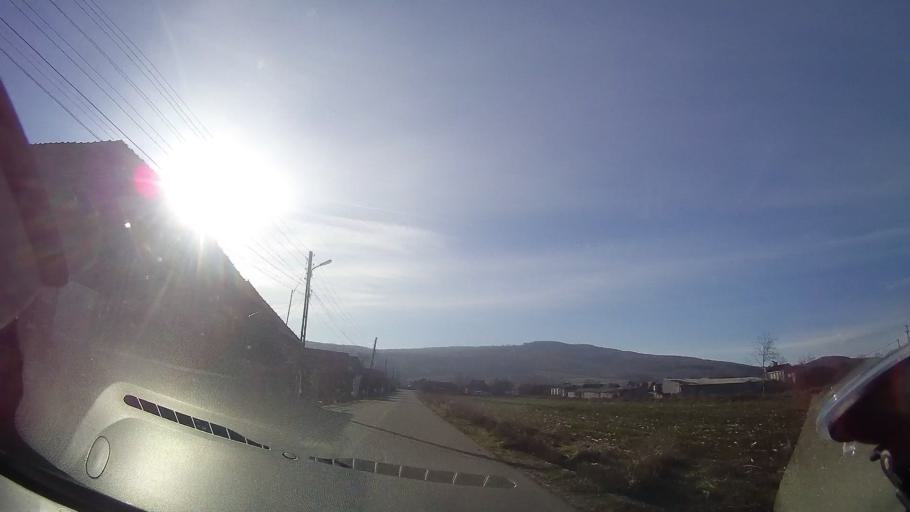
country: RO
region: Bihor
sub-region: Comuna Magesti
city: Magesti
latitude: 47.0104
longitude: 22.4529
